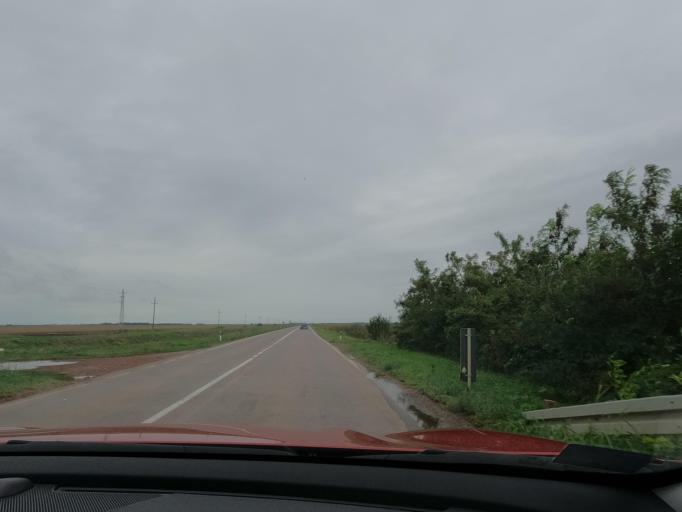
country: RS
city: Banatska Topola
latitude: 45.7201
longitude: 20.4184
